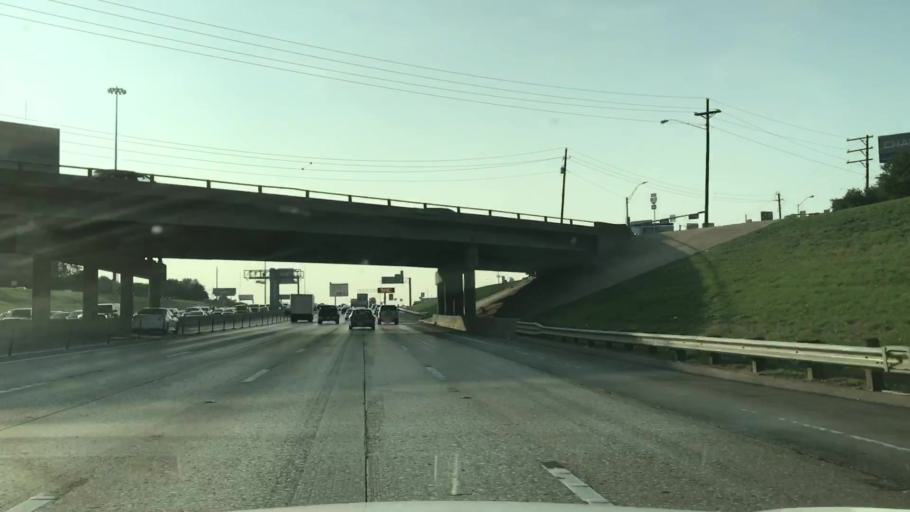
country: US
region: Texas
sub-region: Dallas County
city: Richardson
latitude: 32.9112
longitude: -96.7350
